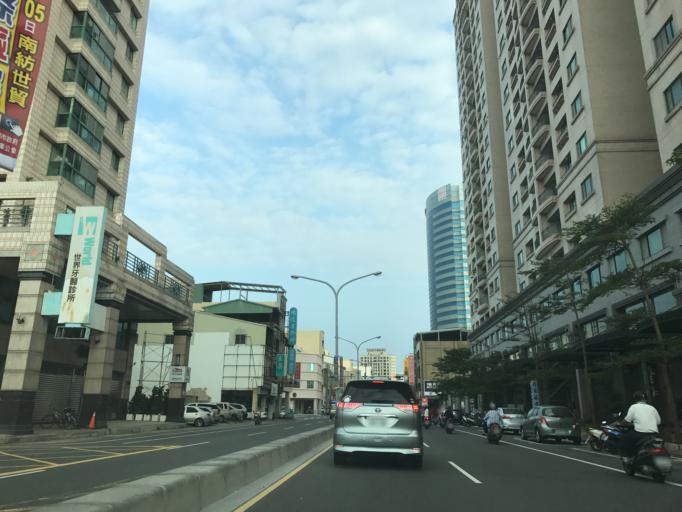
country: TW
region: Taiwan
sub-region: Tainan
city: Tainan
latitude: 22.9976
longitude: 120.1882
